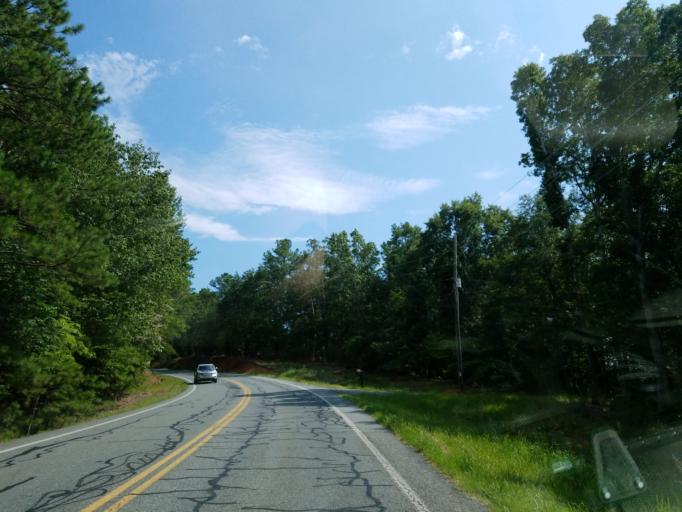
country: US
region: Georgia
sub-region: Gilmer County
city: Ellijay
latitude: 34.5838
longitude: -84.6100
